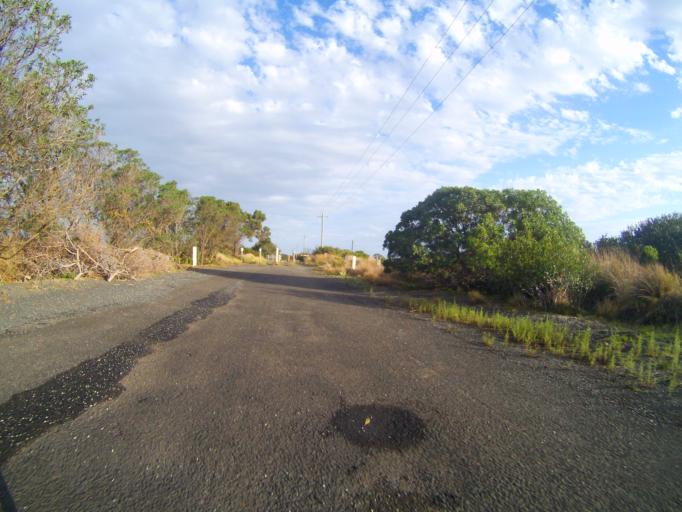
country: AU
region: Victoria
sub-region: Queenscliffe
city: Queenscliff
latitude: -38.2623
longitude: 144.6167
